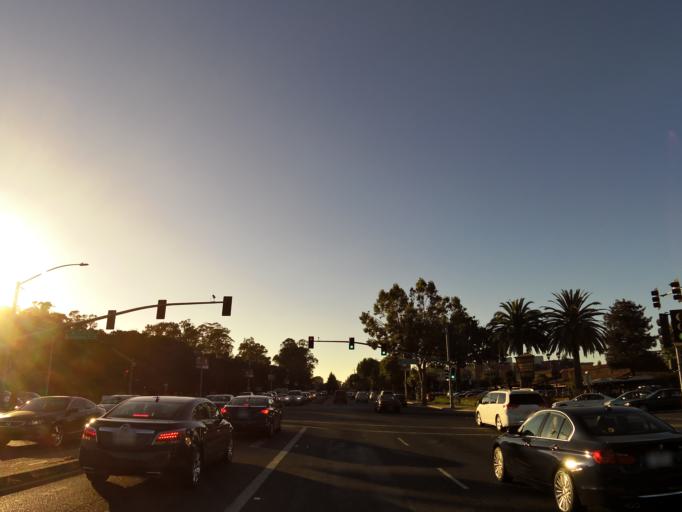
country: US
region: California
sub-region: Santa Clara County
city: Stanford
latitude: 37.4370
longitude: -122.1597
